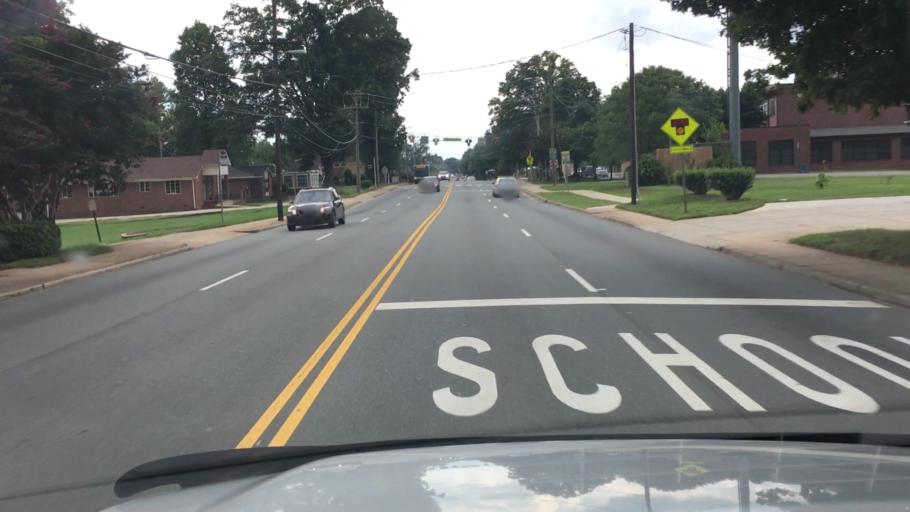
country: US
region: North Carolina
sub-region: Mecklenburg County
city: Charlotte
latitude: 35.2581
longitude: -80.8554
